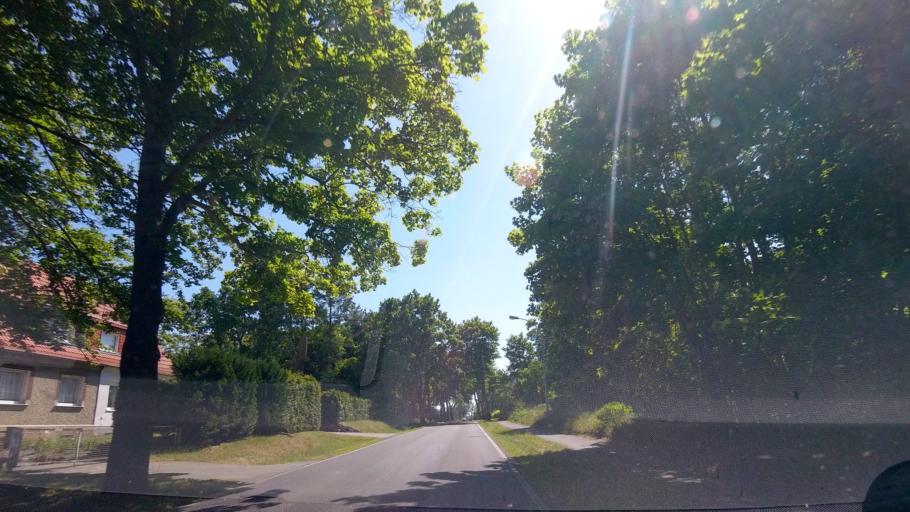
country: DE
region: Brandenburg
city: Gross Kreutz
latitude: 52.3950
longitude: 12.7118
